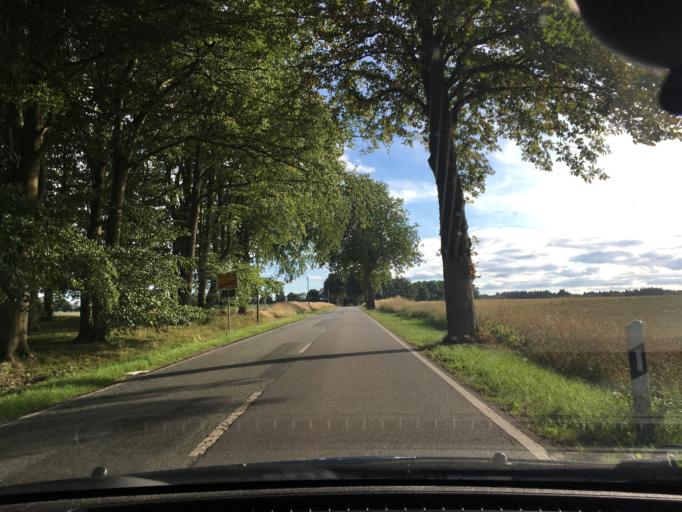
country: DE
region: Lower Saxony
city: Brackel
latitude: 53.3271
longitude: 10.0721
